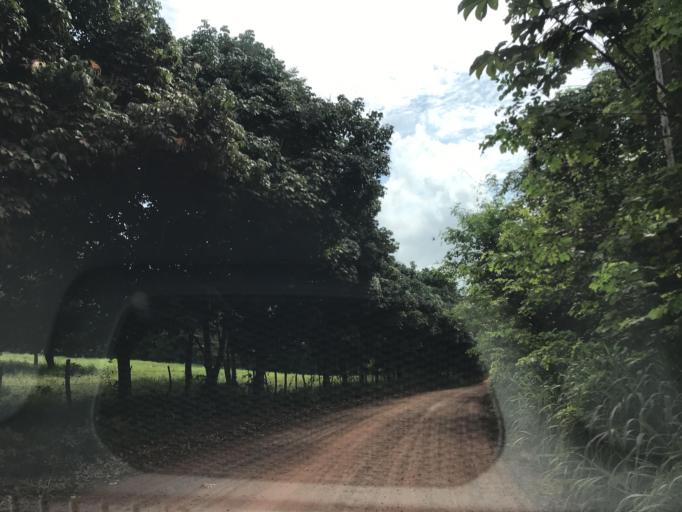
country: BR
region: Bahia
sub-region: Entre Rios
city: Entre Rios
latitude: -12.1646
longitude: -38.1619
